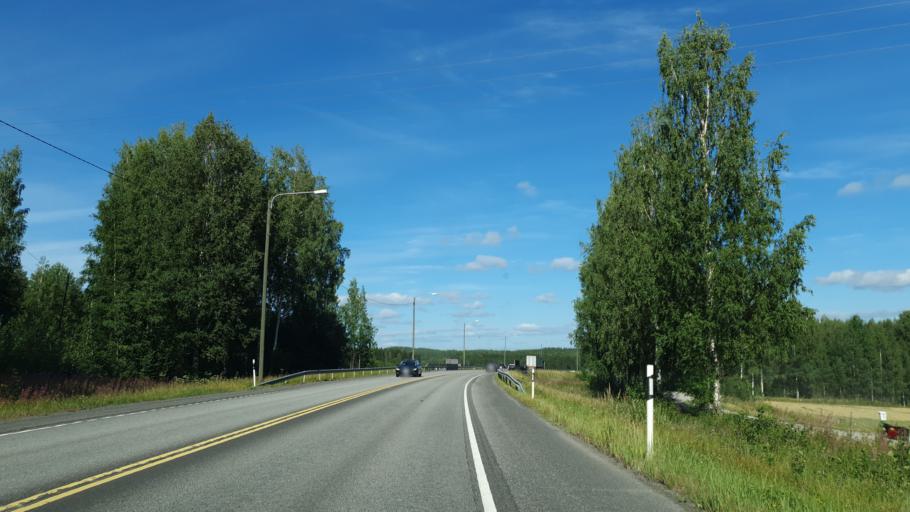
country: FI
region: Central Finland
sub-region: Jyvaeskylae
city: Toivakka
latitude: 62.2422
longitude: 25.9847
